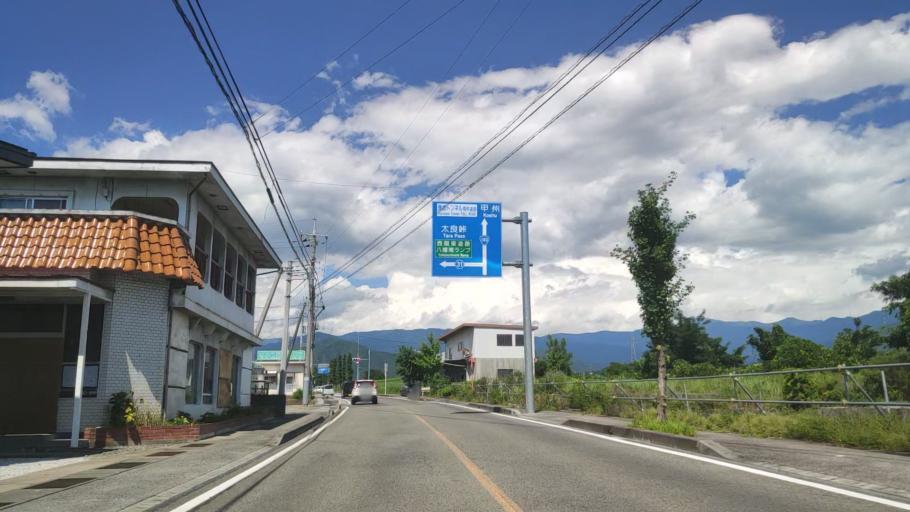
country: JP
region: Yamanashi
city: Enzan
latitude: 35.7006
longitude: 138.6901
